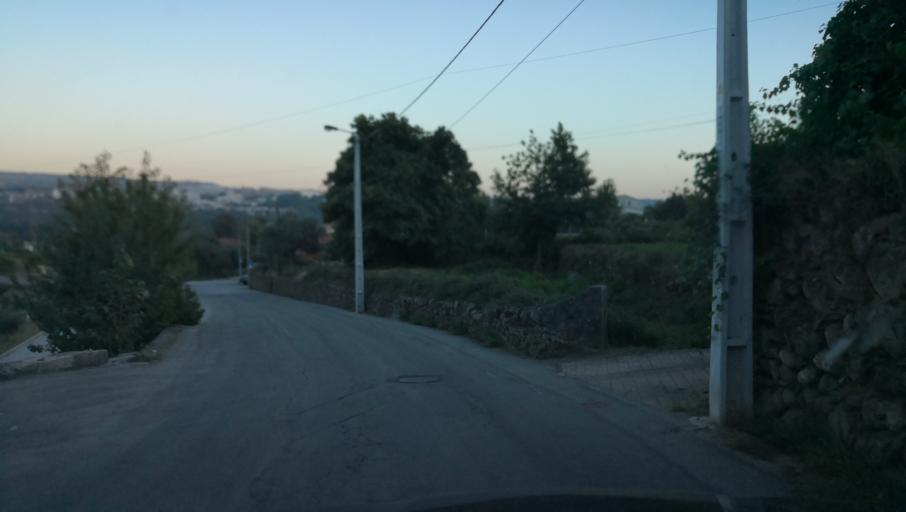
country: PT
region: Vila Real
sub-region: Vila Real
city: Vila Real
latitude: 41.3166
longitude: -7.7675
